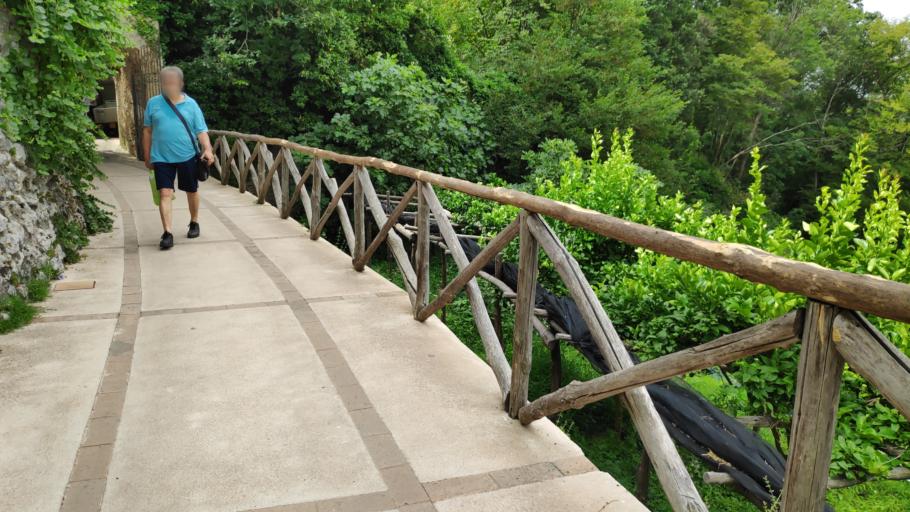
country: IT
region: Campania
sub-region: Provincia di Salerno
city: Ravello
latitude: 40.6451
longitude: 14.6104
